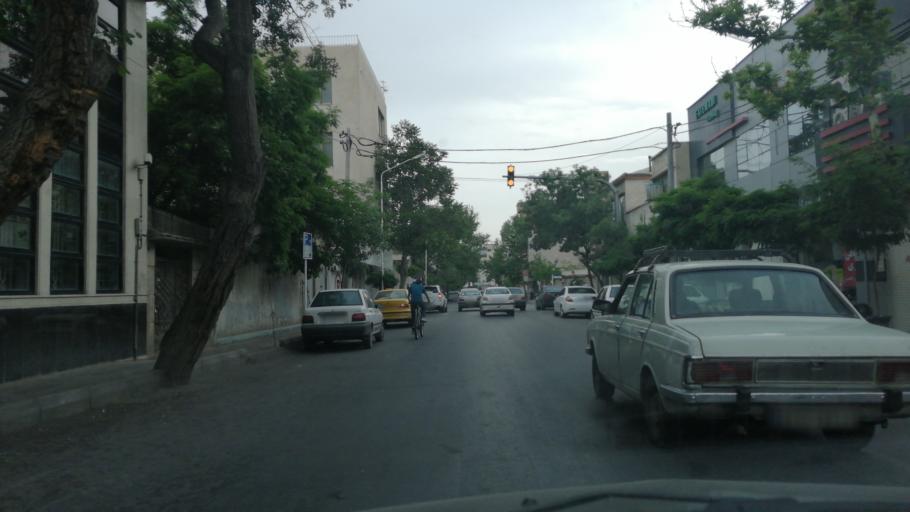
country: IR
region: Razavi Khorasan
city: Mashhad
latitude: 36.2974
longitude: 59.5835
